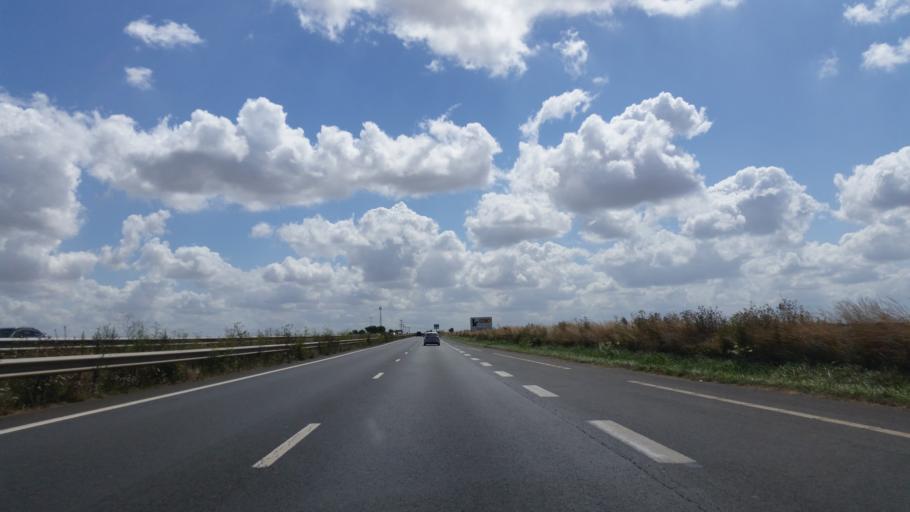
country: FR
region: Lower Normandy
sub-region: Departement du Calvados
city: Bourguebus
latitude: 49.1206
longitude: -0.3247
